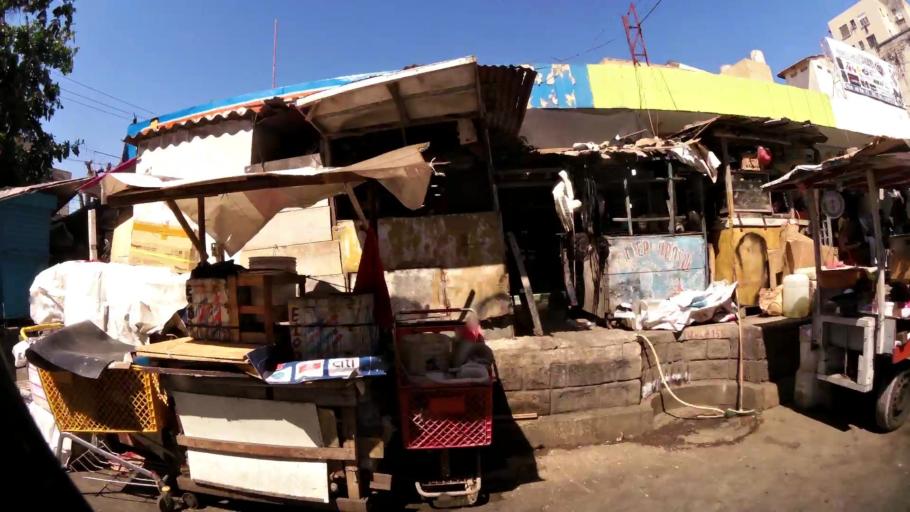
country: CO
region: Atlantico
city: Barranquilla
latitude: 10.9800
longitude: -74.7810
